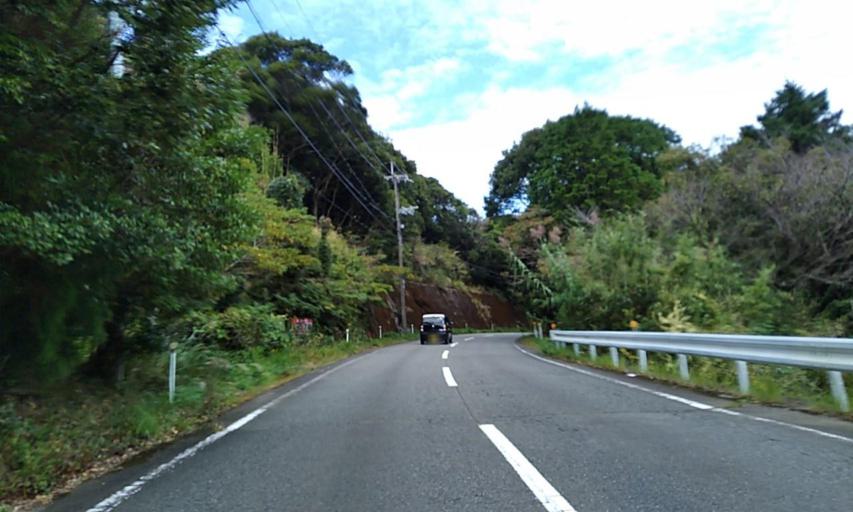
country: JP
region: Wakayama
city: Shingu
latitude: 33.4680
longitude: 135.8306
